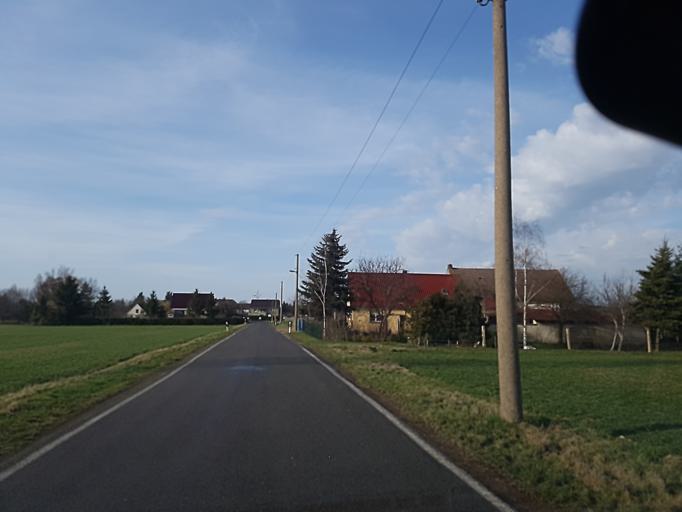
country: DE
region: Brandenburg
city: Falkenberg
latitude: 51.5452
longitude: 13.2946
